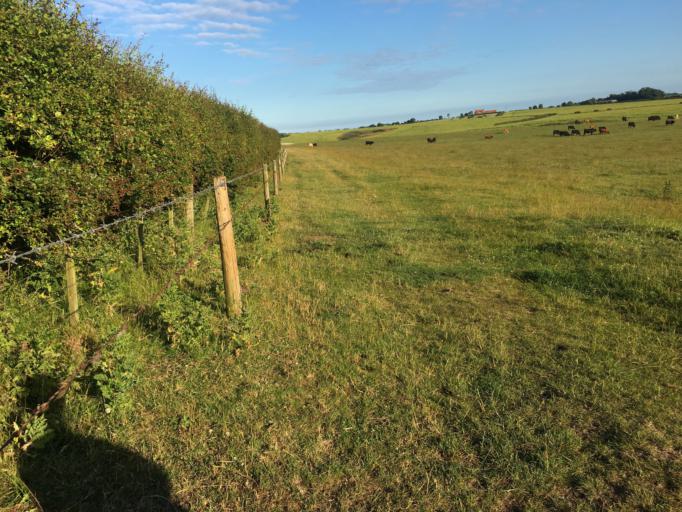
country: GB
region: England
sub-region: Northumberland
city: Bamburgh
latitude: 55.5985
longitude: -1.6960
